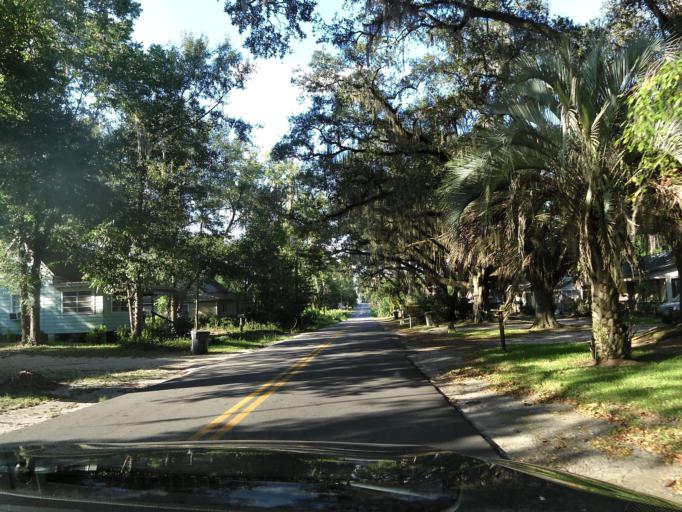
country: US
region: Georgia
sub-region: Brooks County
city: Quitman
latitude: 30.7802
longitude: -83.5529
